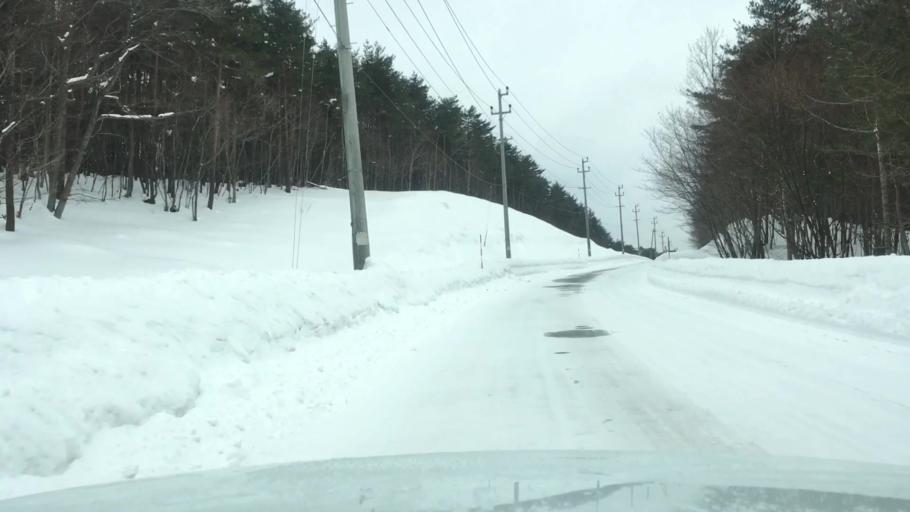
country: JP
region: Iwate
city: Shizukuishi
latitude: 39.9795
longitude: 141.0008
